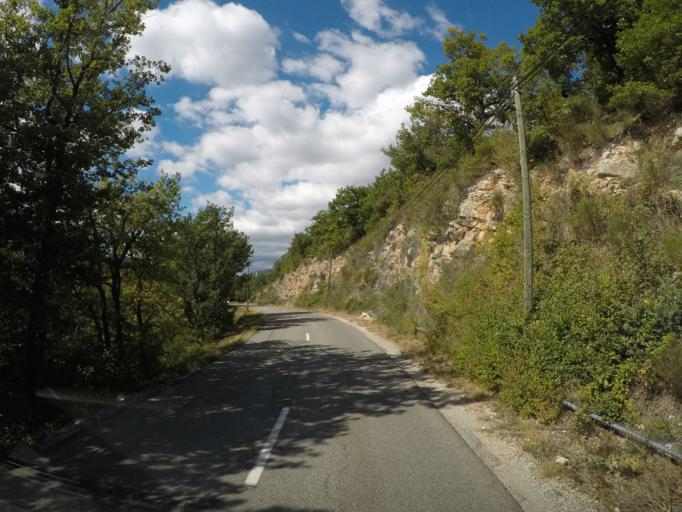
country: FR
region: Provence-Alpes-Cote d'Azur
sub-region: Departement des Hautes-Alpes
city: Laragne-Monteglin
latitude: 44.1731
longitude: 5.7253
